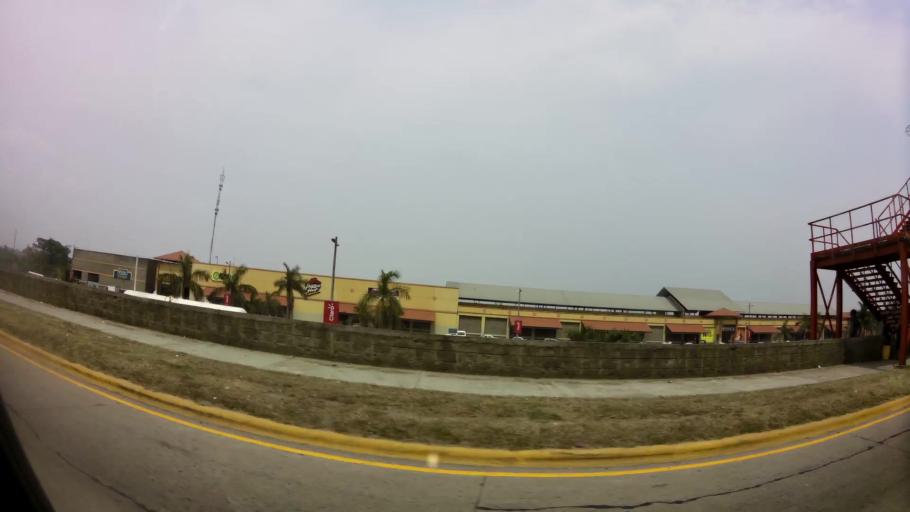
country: HN
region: Cortes
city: Armenta
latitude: 15.4717
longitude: -88.0336
